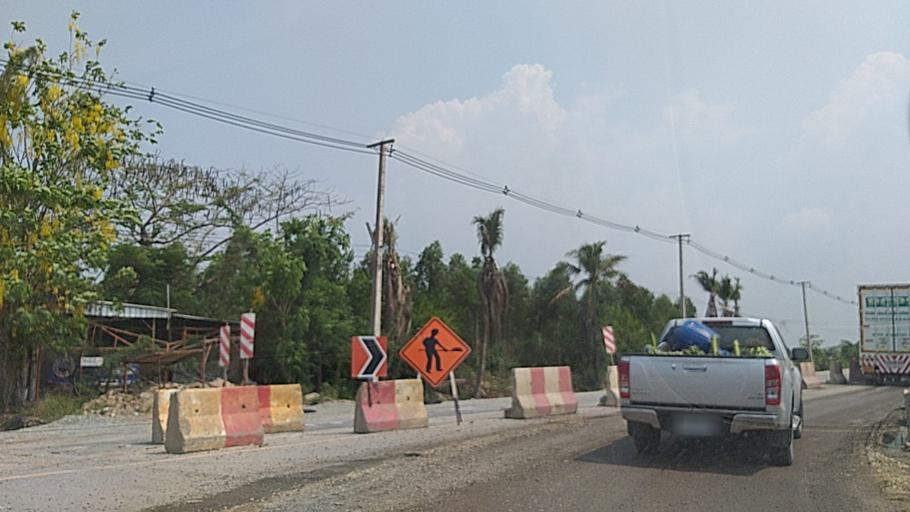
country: TH
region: Chon Buri
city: Phanat Nikhom
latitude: 13.4089
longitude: 101.1895
